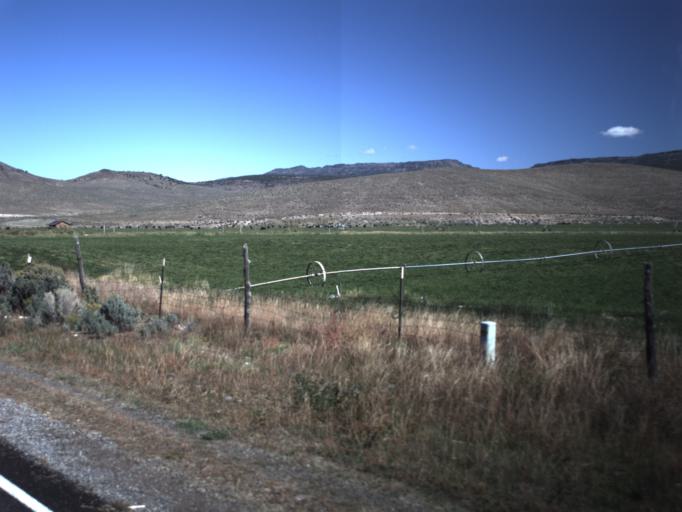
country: US
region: Utah
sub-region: Piute County
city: Junction
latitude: 38.0940
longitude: -111.9833
